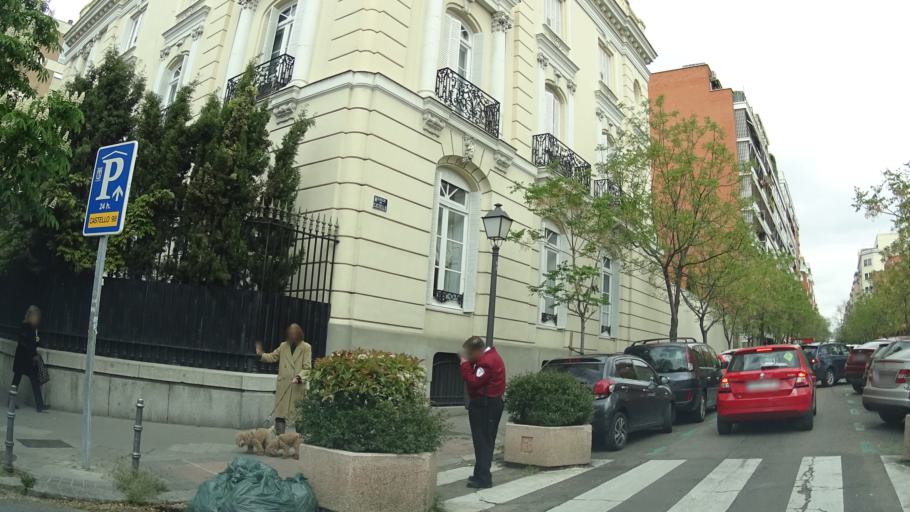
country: ES
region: Madrid
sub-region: Provincia de Madrid
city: Salamanca
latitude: 40.4315
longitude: -3.6810
